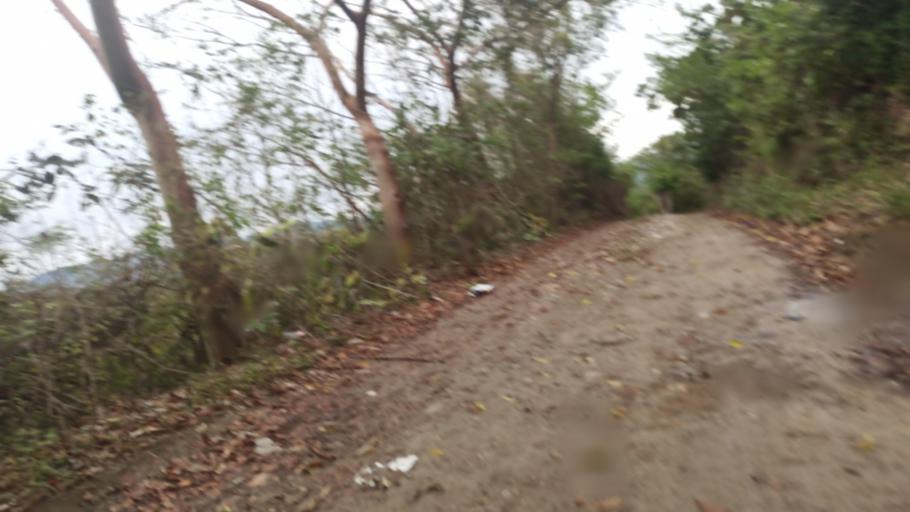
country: MX
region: Veracruz
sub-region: Papantla
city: El Chote
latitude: 20.3854
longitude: -97.3547
